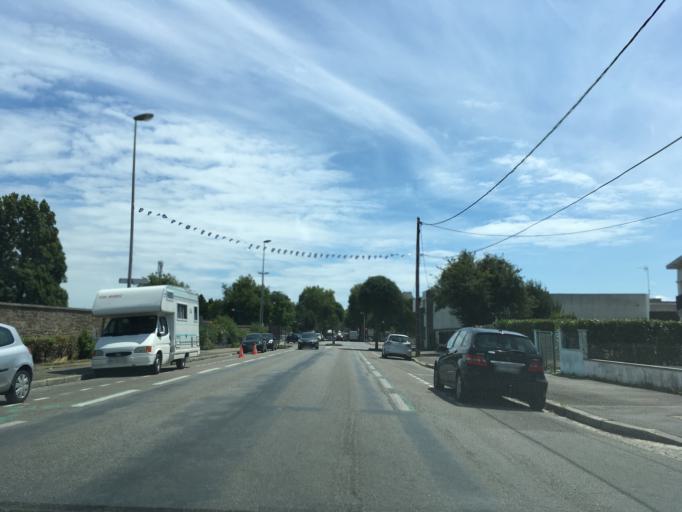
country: FR
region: Brittany
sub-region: Departement du Morbihan
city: Lorient
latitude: 47.7370
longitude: -3.3674
